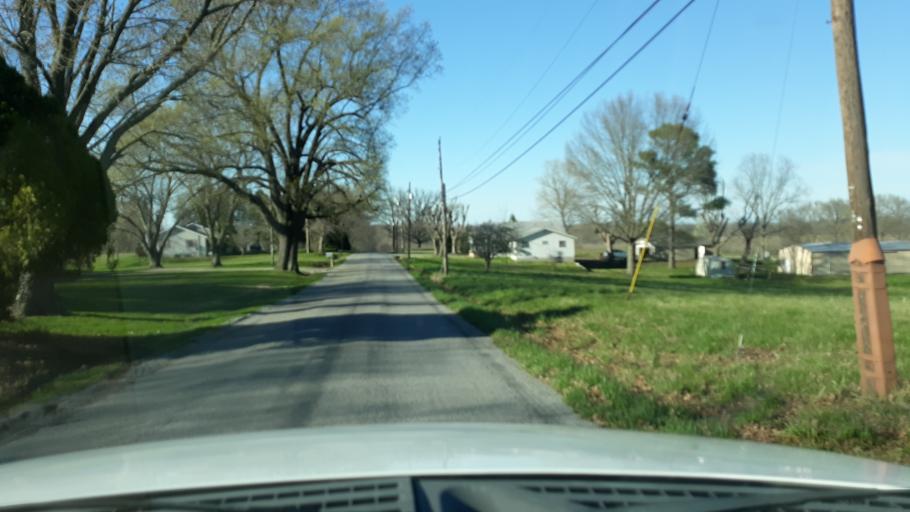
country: US
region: Illinois
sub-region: Saline County
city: Harrisburg
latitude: 37.7523
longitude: -88.5680
